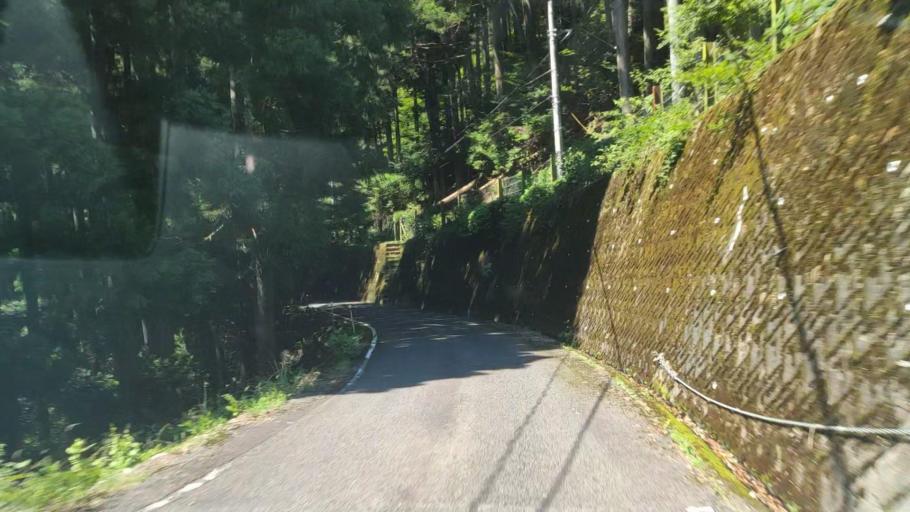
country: JP
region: Gifu
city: Godo
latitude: 35.6934
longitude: 136.5733
